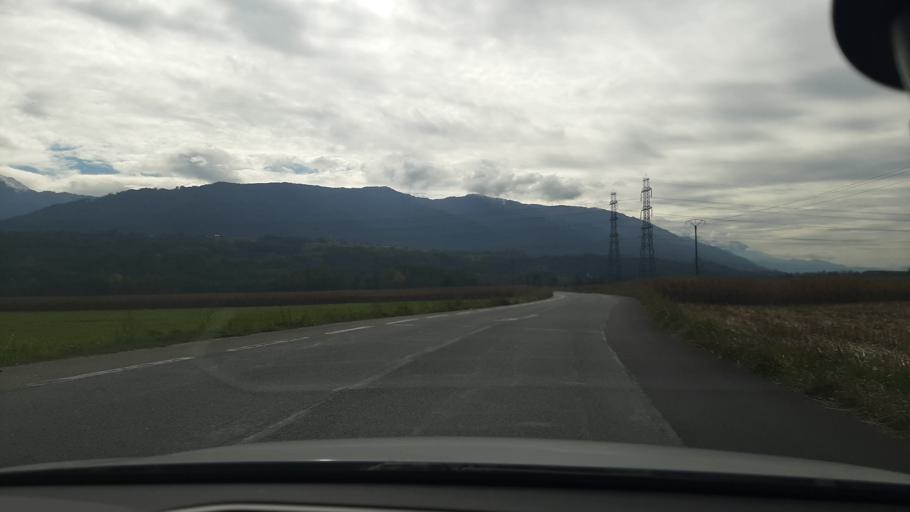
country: FR
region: Rhone-Alpes
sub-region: Departement de la Savoie
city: Montmelian
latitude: 45.4700
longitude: 6.0441
